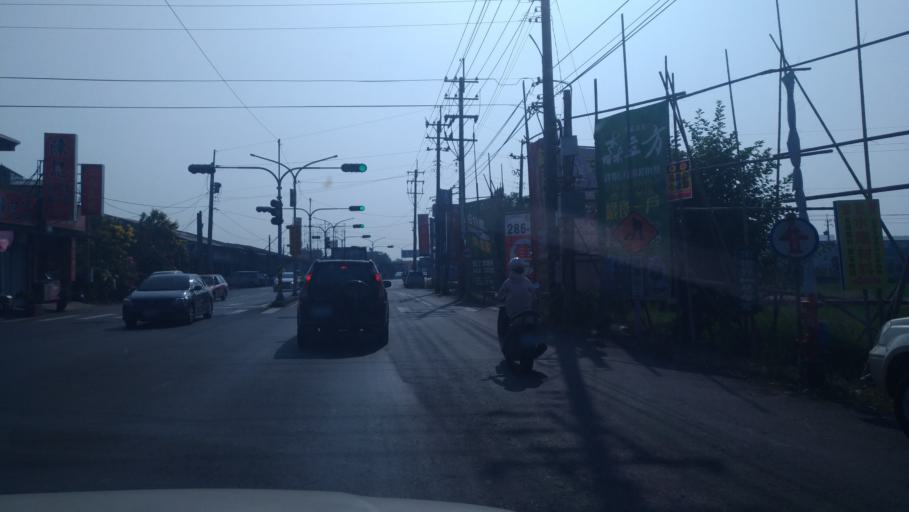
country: TW
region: Taiwan
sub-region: Chiayi
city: Jiayi Shi
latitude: 23.5144
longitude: 120.4308
